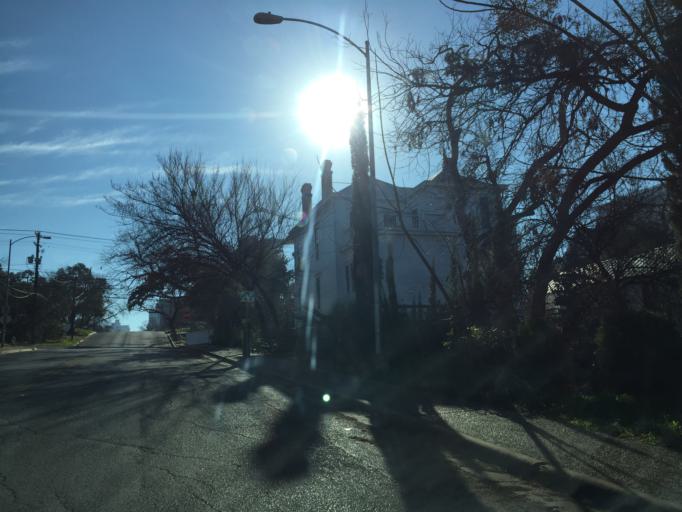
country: US
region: Texas
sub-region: Travis County
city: Austin
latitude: 30.2733
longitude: -97.7503
